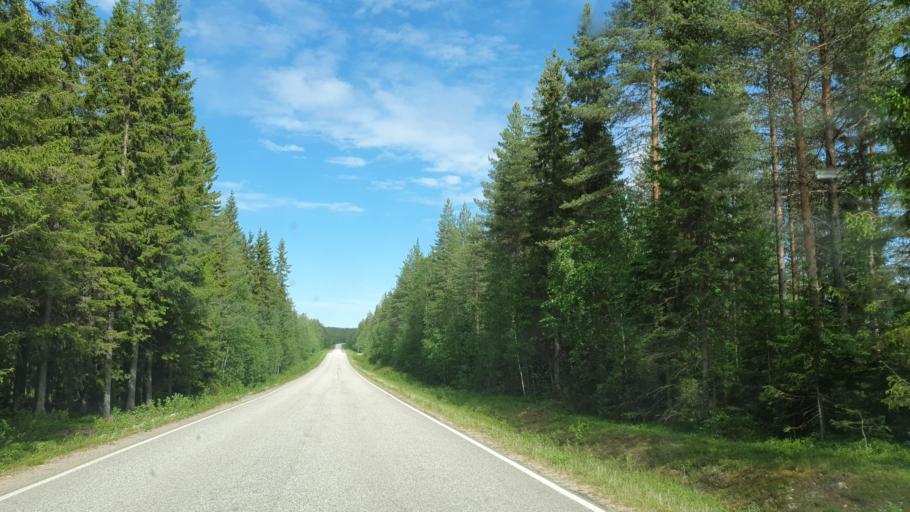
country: FI
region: Kainuu
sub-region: Kehys-Kainuu
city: Suomussalmi
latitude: 64.5889
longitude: 29.0718
